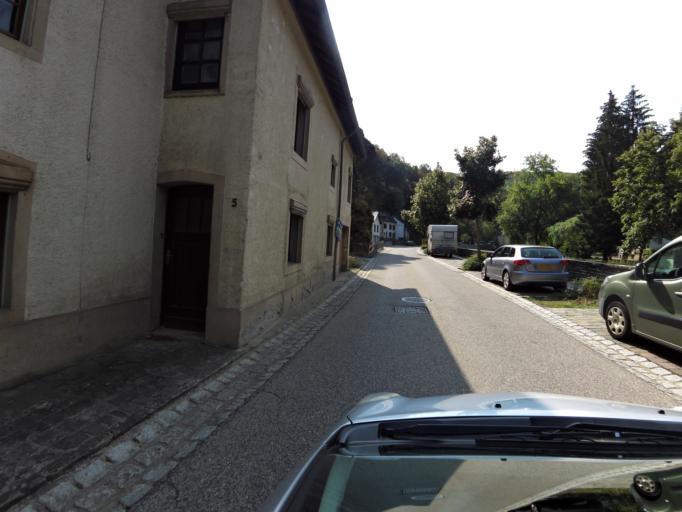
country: LU
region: Diekirch
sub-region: Canton de Wiltz
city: Esch-sur-Sure
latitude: 49.9111
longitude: 5.9336
